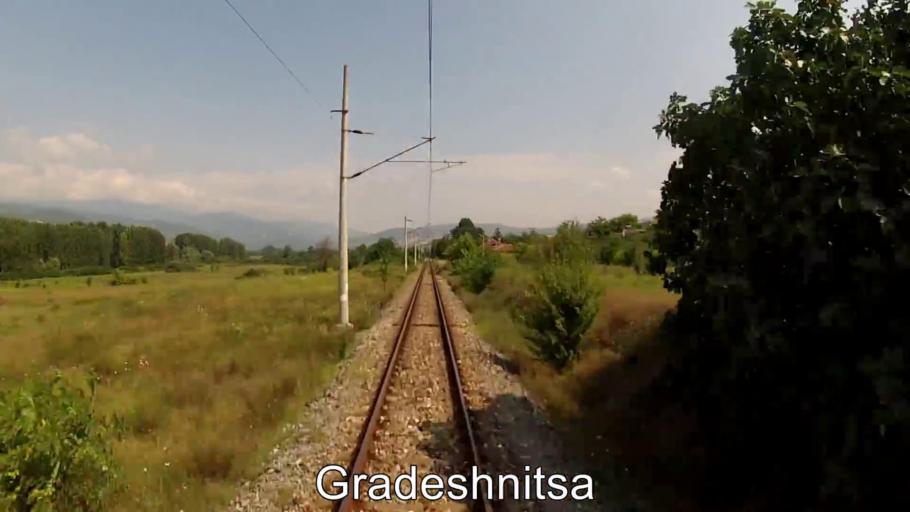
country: BG
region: Blagoevgrad
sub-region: Obshtina Strumyani
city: Strumyani
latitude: 41.6565
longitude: 23.1786
